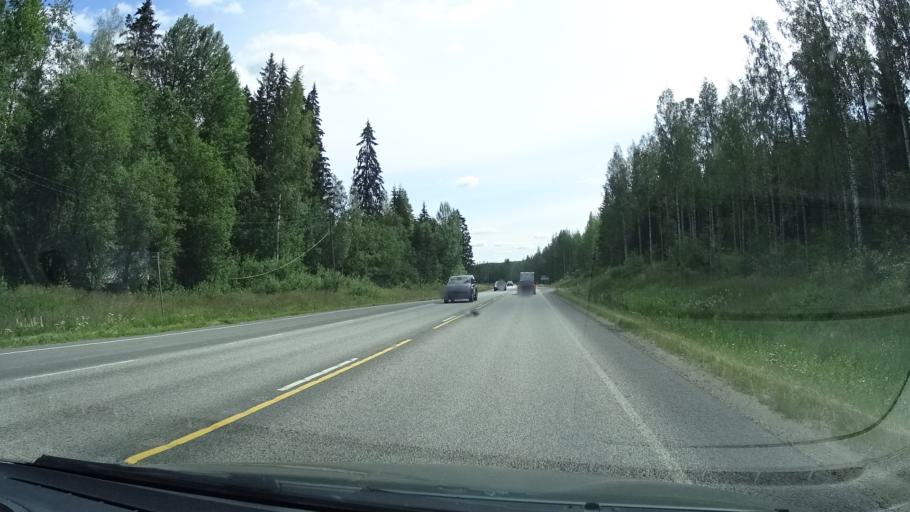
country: FI
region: Central Finland
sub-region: Jyvaeskylae
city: Jyvaeskylae
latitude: 62.2628
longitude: 25.5889
